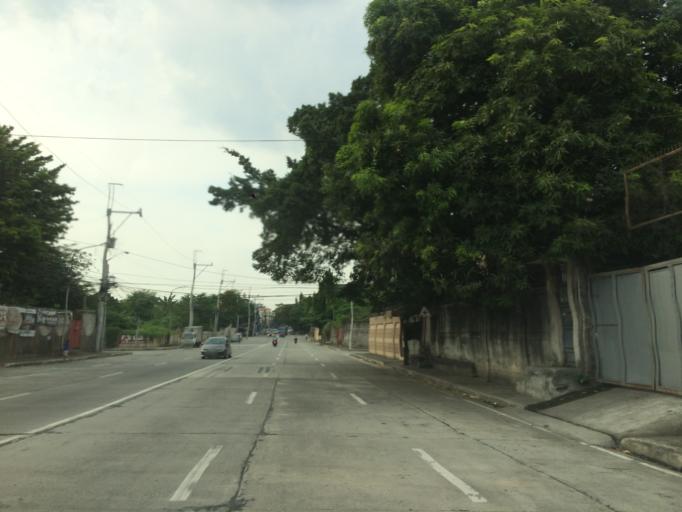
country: PH
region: Calabarzon
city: Del Monte
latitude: 14.6315
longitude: 121.0076
